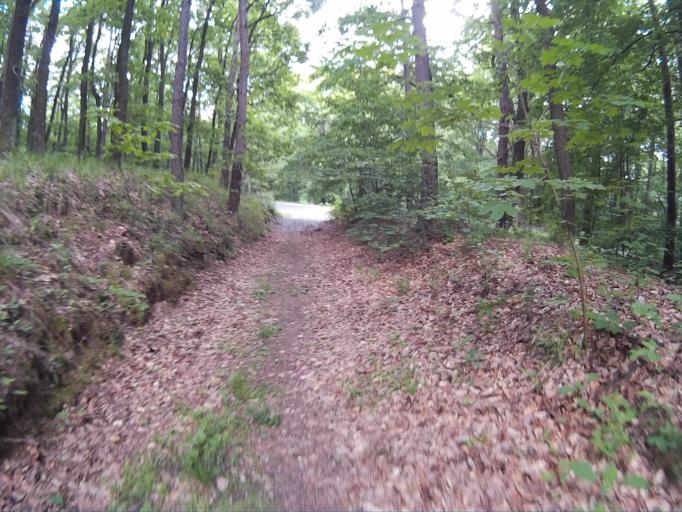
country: HU
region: Vas
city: Koszeg
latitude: 47.3722
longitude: 16.5093
